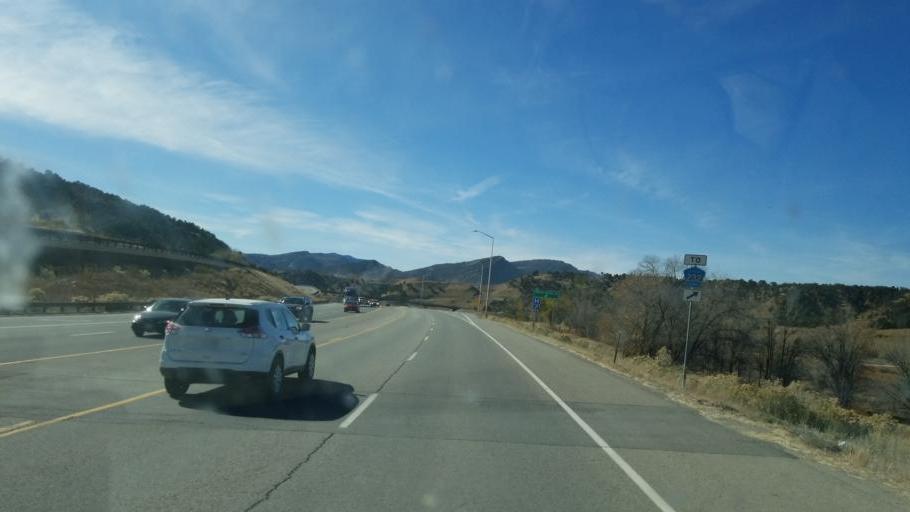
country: US
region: Colorado
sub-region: La Plata County
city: Durango
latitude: 37.2292
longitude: -107.8310
